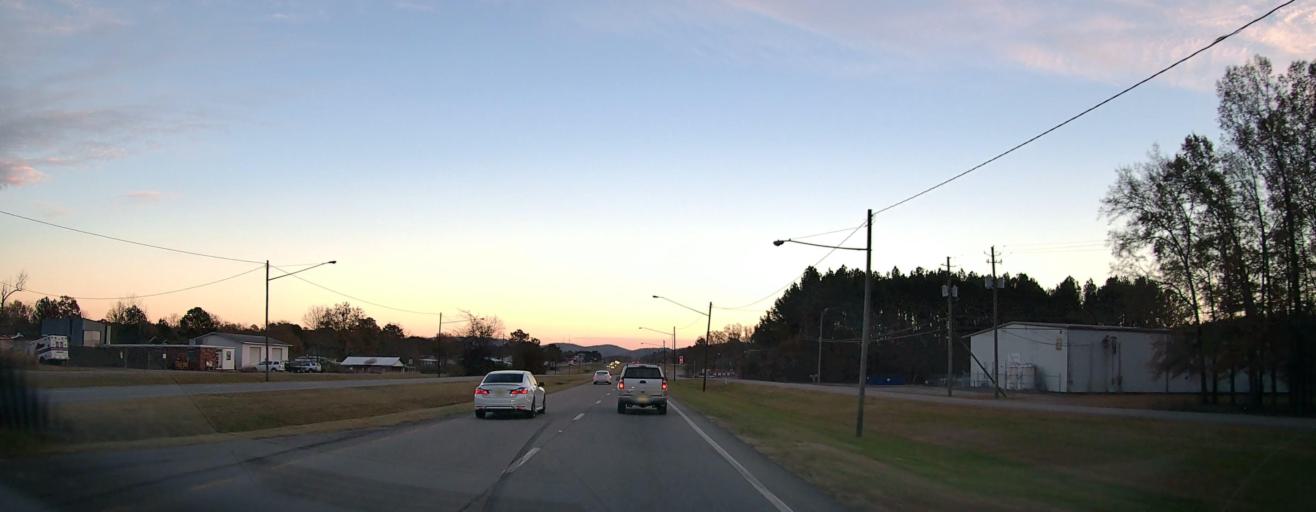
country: US
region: Alabama
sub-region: Etowah County
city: Glencoe
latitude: 33.9793
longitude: -85.9564
